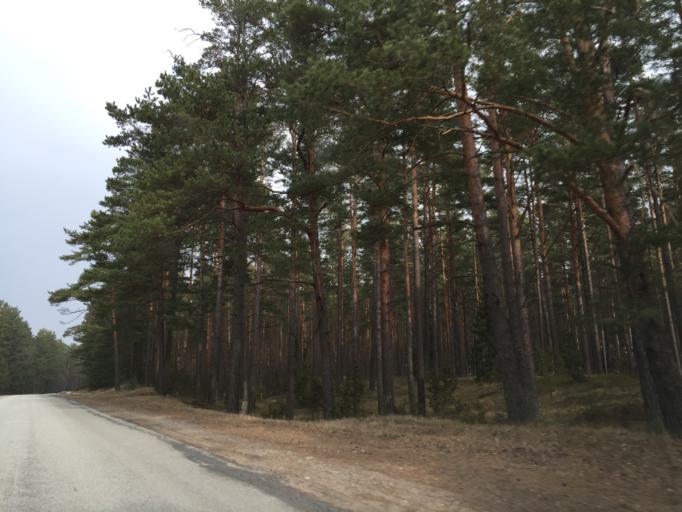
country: LV
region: Salacgrivas
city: Ainazi
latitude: 57.9675
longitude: 24.4081
